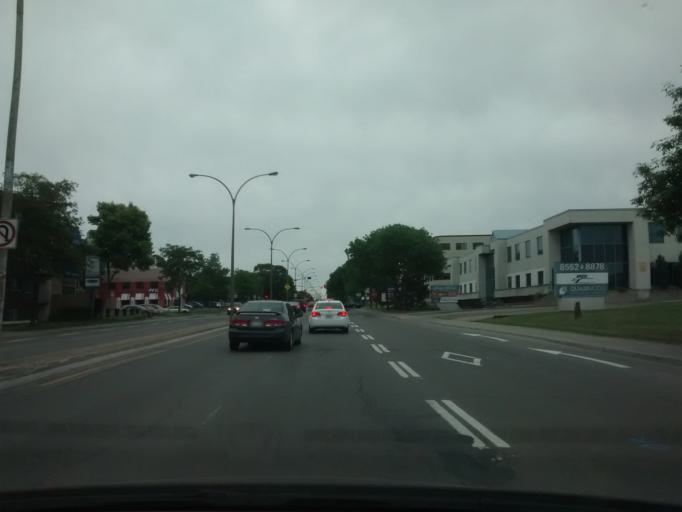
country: CA
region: Quebec
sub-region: Montreal
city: Saint-Leonard
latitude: 45.5761
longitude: -73.6132
